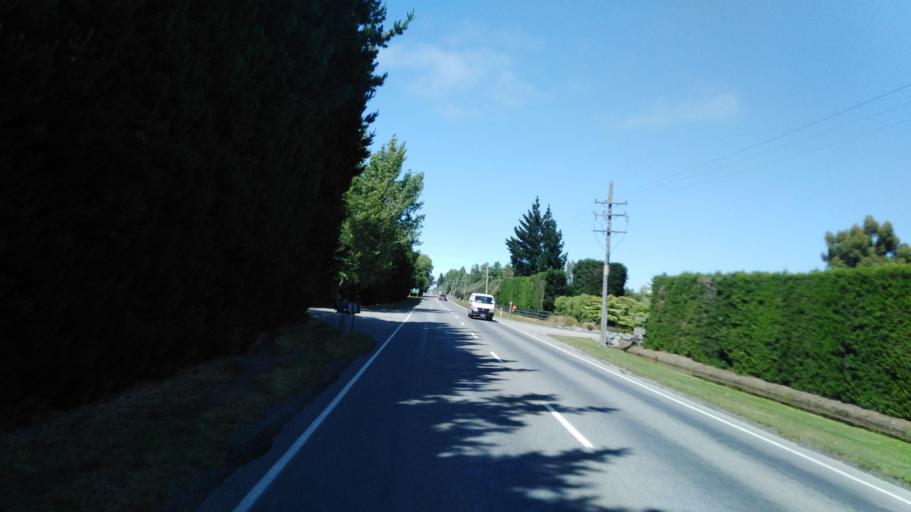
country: NZ
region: Canterbury
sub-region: Selwyn District
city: Prebbleton
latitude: -43.5164
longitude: 172.5067
